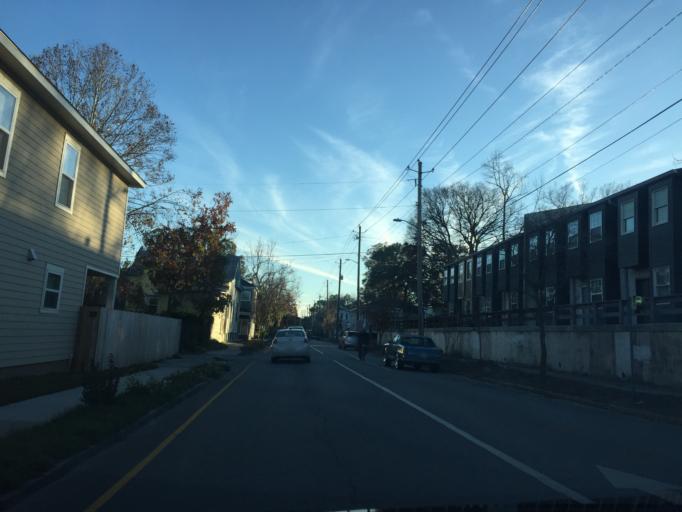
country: US
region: Georgia
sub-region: Chatham County
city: Savannah
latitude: 32.0596
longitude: -81.0934
